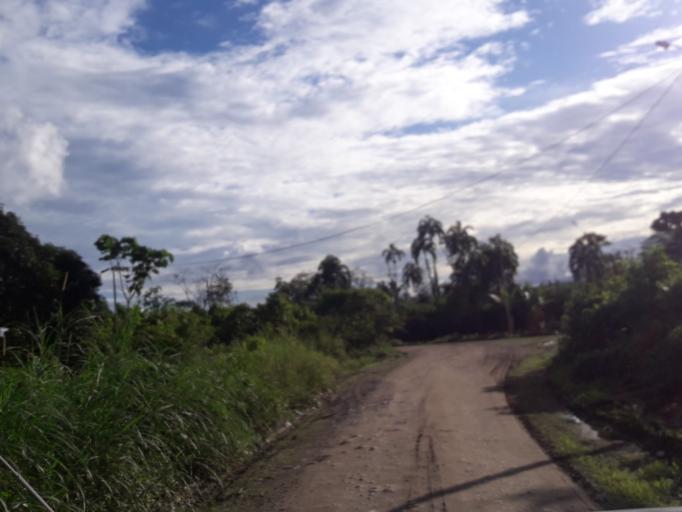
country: EC
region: Orellana
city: Boca Suno
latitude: -0.8837
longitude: -77.2956
